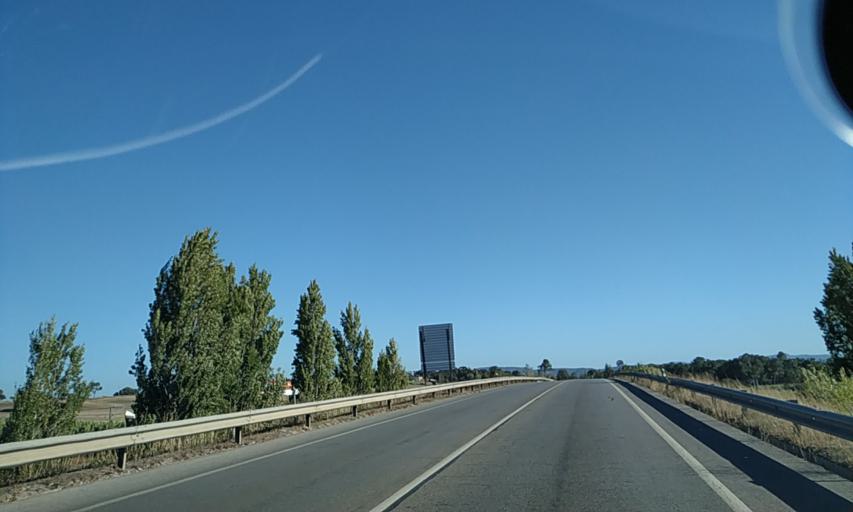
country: PT
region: Setubal
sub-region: Moita
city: Moita
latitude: 38.6413
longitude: -8.9718
